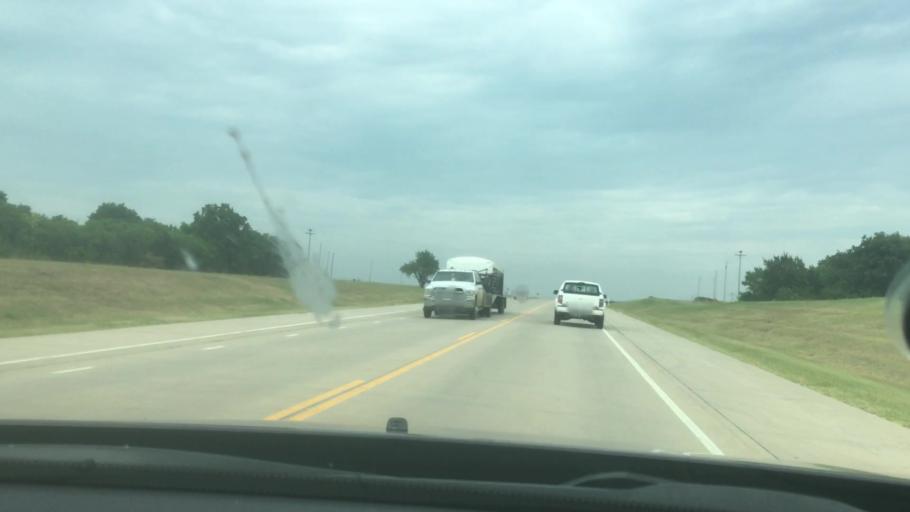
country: US
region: Oklahoma
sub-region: Murray County
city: Sulphur
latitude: 34.6167
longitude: -96.8700
